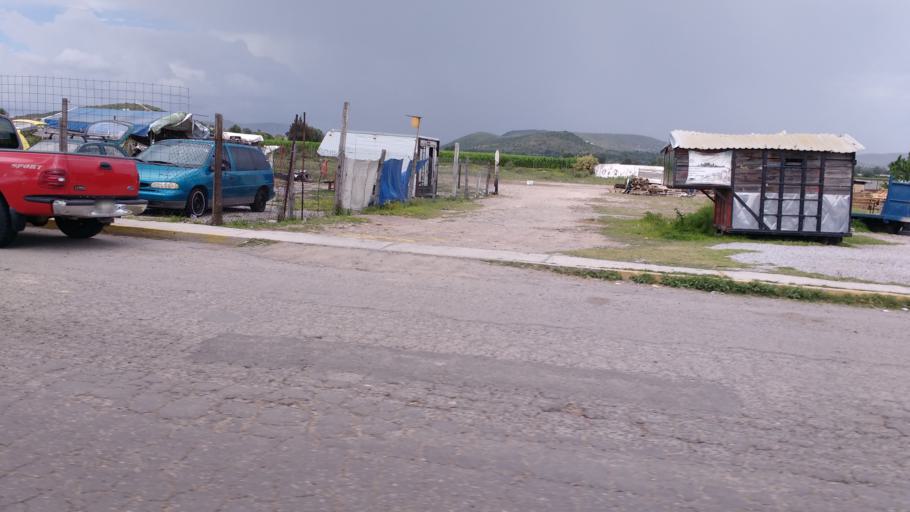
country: MX
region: Hidalgo
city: Tlahuelilpan
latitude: 20.1394
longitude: -99.2349
